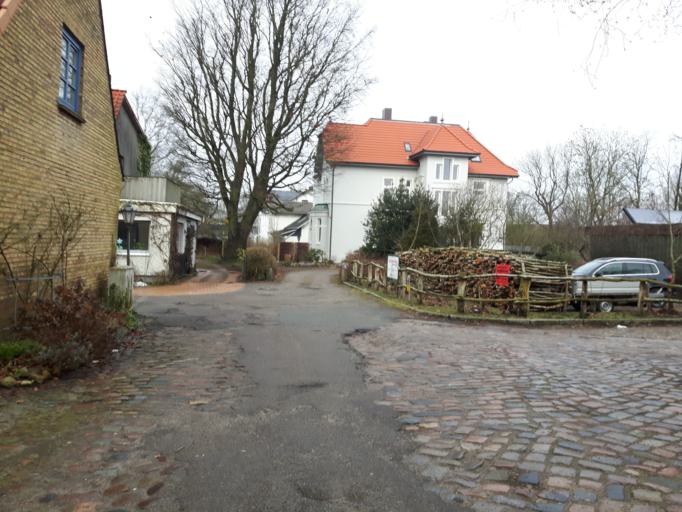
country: DE
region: Schleswig-Holstein
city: Busdorf
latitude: 54.5057
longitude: 9.5429
